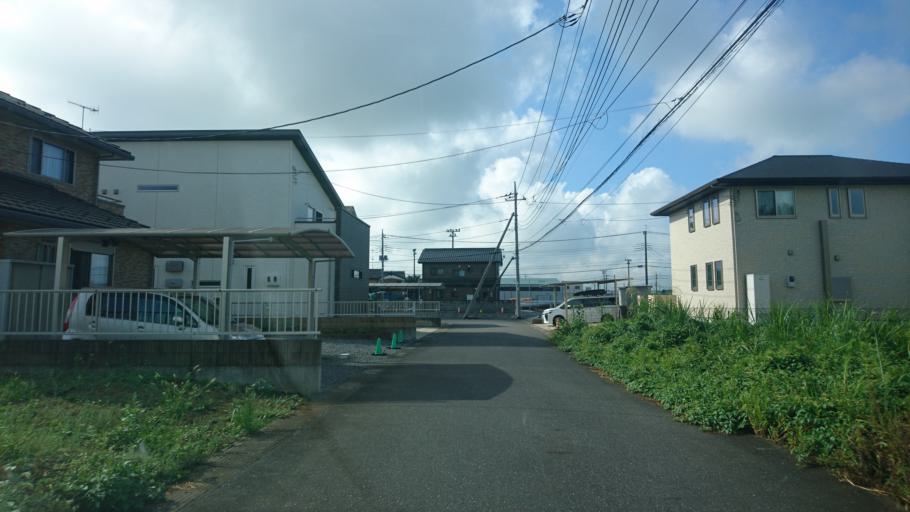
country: JP
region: Tochigi
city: Sano
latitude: 36.2951
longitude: 139.5990
